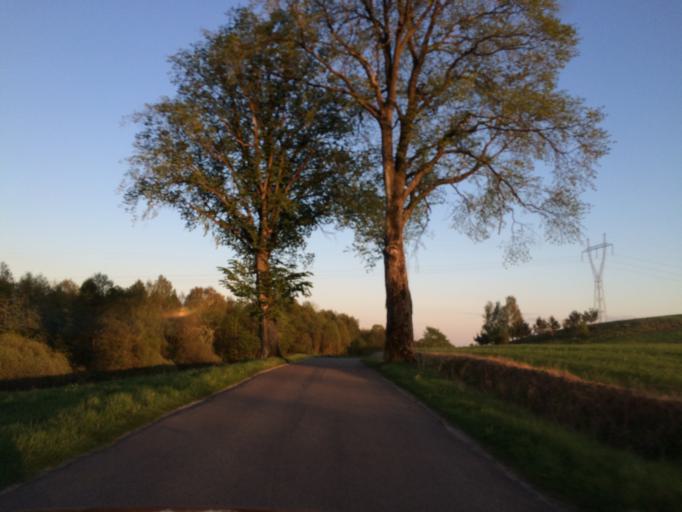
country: PL
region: Warmian-Masurian Voivodeship
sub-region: Powiat dzialdowski
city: Rybno
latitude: 53.4278
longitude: 19.9193
